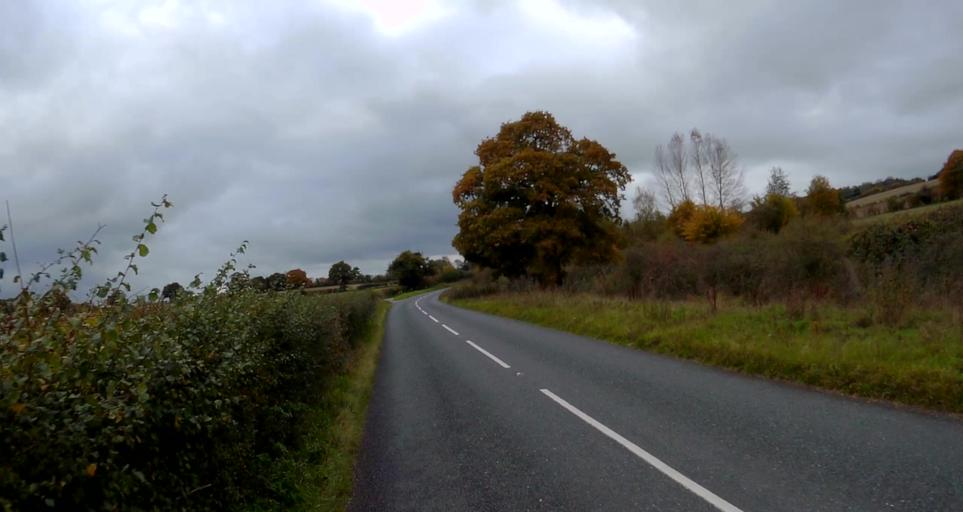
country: GB
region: England
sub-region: Hampshire
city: Four Marks
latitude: 51.1613
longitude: -1.1444
